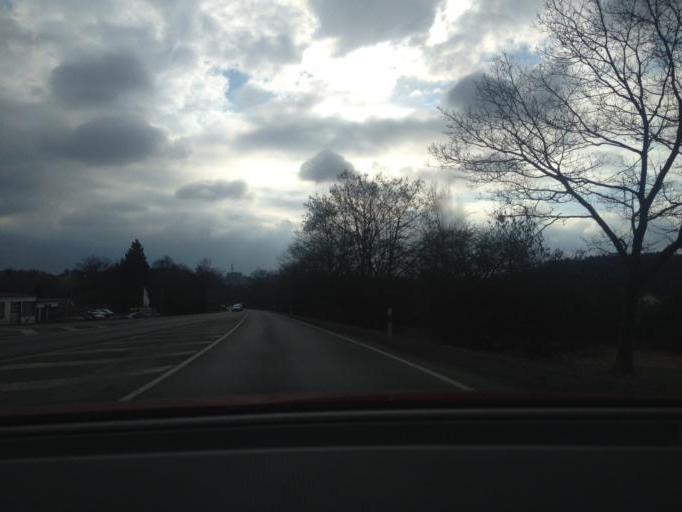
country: DE
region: Bavaria
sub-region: Upper Franconia
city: Dohlau
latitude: 50.2864
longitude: 11.9258
